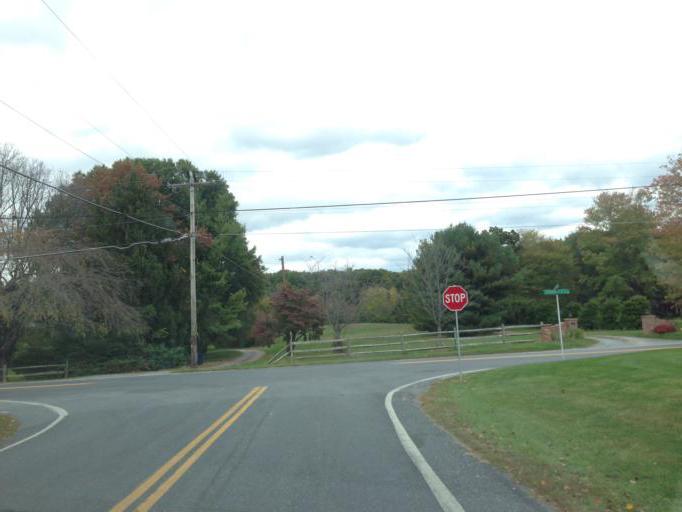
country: US
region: Maryland
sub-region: Carroll County
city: Mount Airy
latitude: 39.2841
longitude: -77.0907
